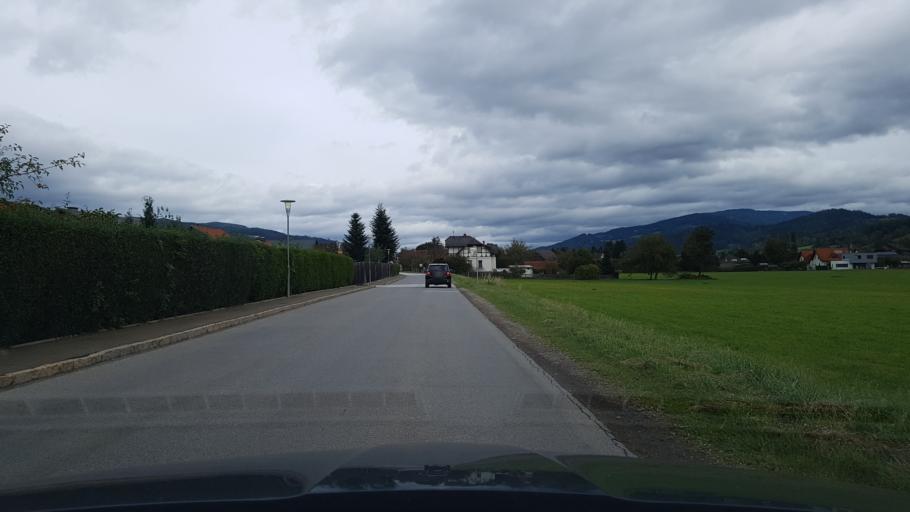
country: AT
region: Styria
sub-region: Politischer Bezirk Bruck-Muerzzuschlag
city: Sankt Marein im Muerztal
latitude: 47.4692
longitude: 15.3666
